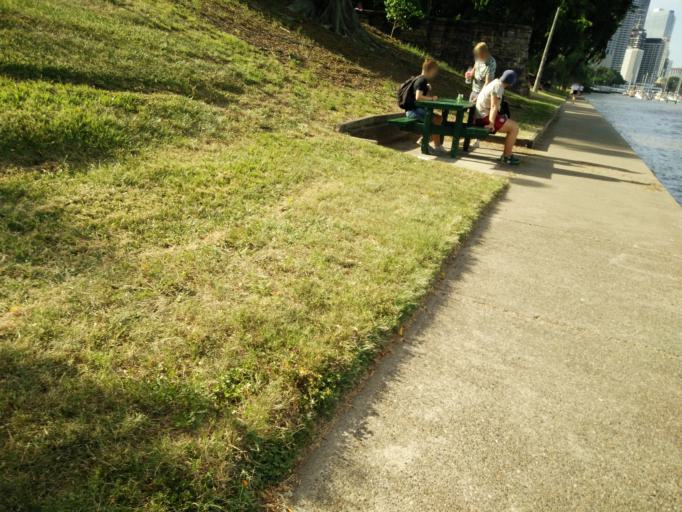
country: AU
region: Queensland
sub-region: Brisbane
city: Brisbane
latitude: -27.4764
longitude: 153.0317
